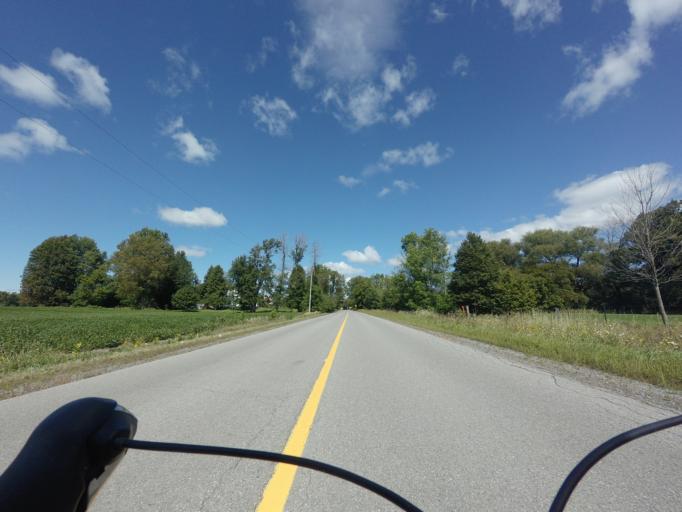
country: CA
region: Ontario
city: Bells Corners
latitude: 45.2511
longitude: -75.8090
